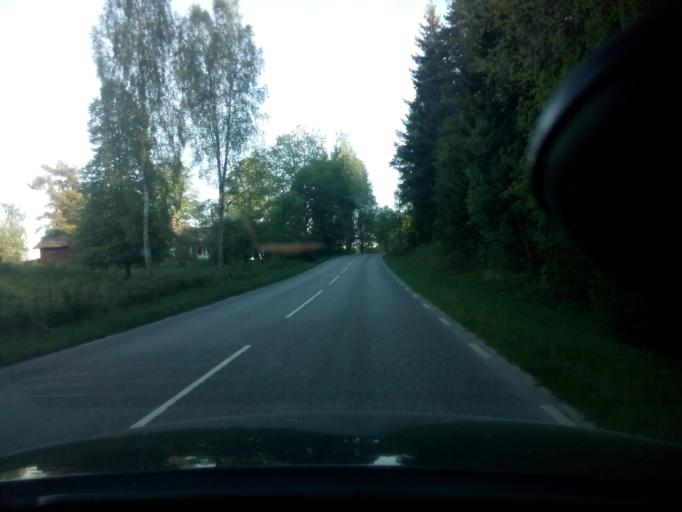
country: SE
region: Soedermanland
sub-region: Nykopings Kommun
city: Nykoping
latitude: 58.7968
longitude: 17.0029
